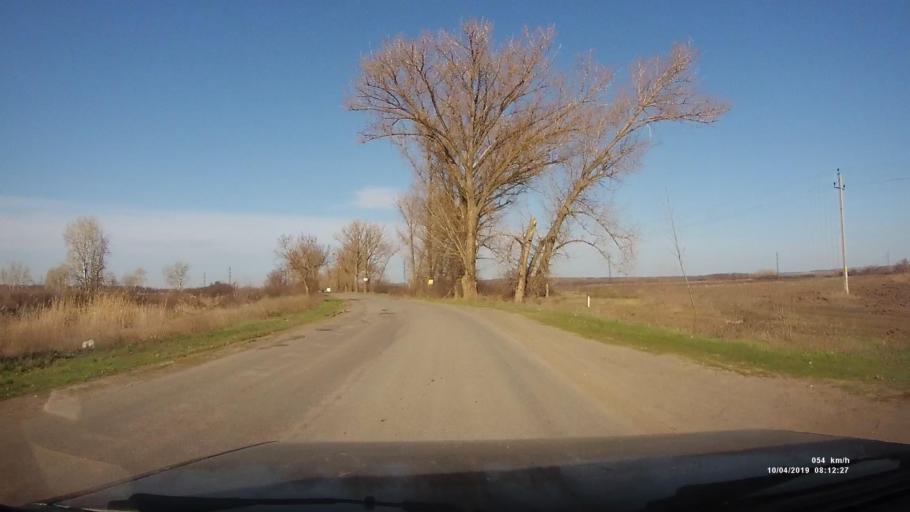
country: RU
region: Rostov
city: Masalovka
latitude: 48.3623
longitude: 40.2575
